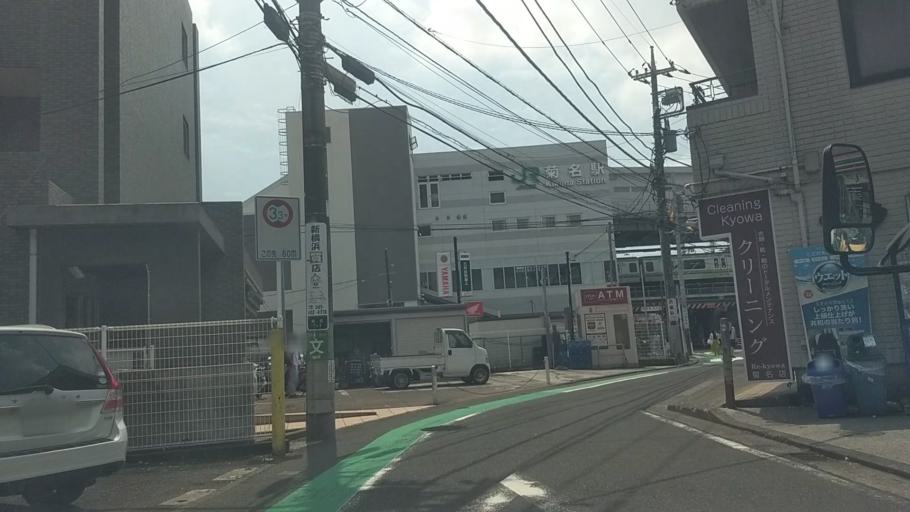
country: JP
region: Kanagawa
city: Yokohama
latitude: 35.5104
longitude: 139.6309
